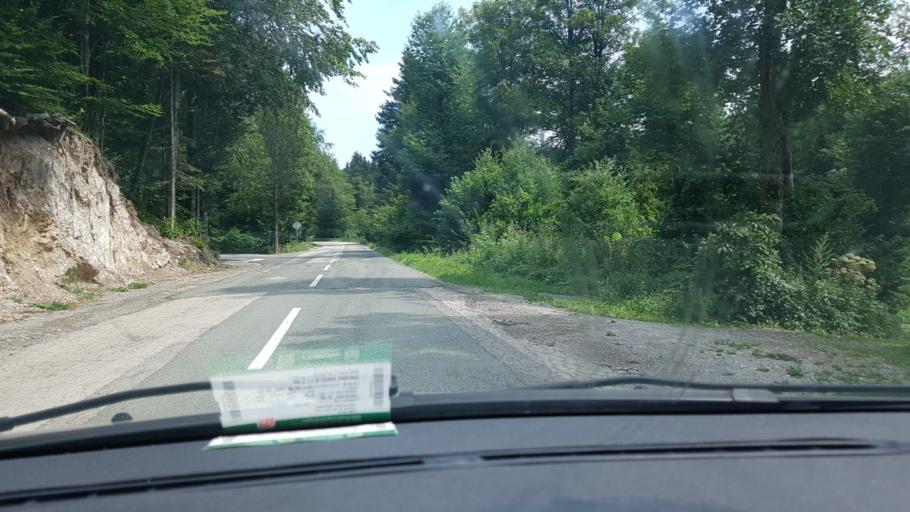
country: HR
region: Primorsko-Goranska
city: Hreljin
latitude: 45.3315
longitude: 14.6908
